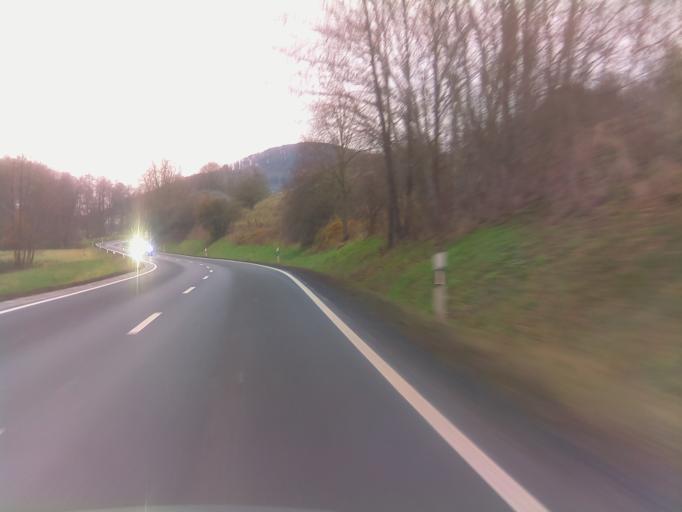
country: DE
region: Thuringia
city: Vacha
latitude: 50.8101
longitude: 10.0080
